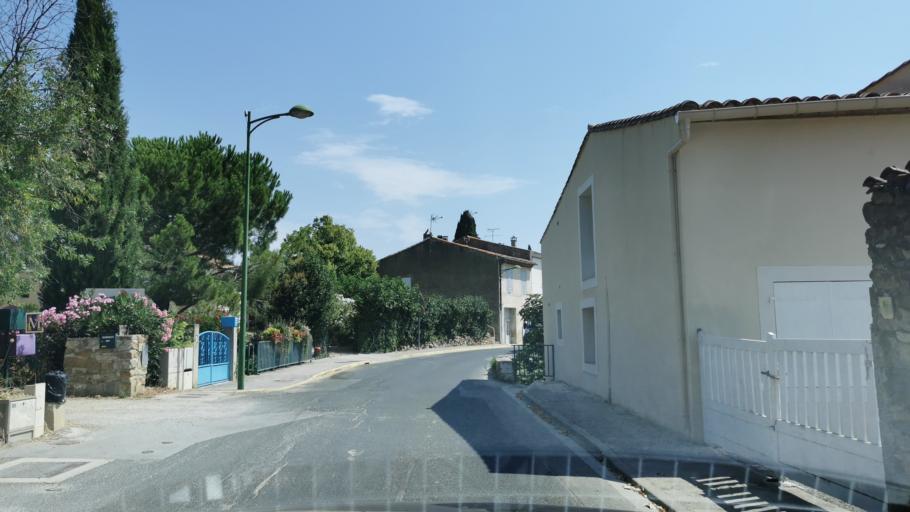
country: FR
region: Languedoc-Roussillon
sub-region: Departement de l'Aude
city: Bize-Minervois
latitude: 43.3180
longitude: 2.8683
